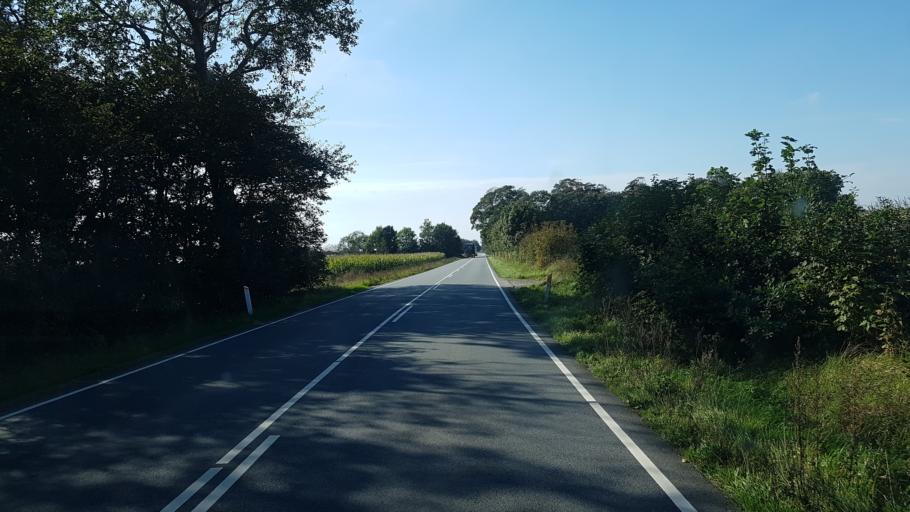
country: DK
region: South Denmark
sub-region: Vejen Kommune
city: Vejen
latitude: 55.4508
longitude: 9.1492
